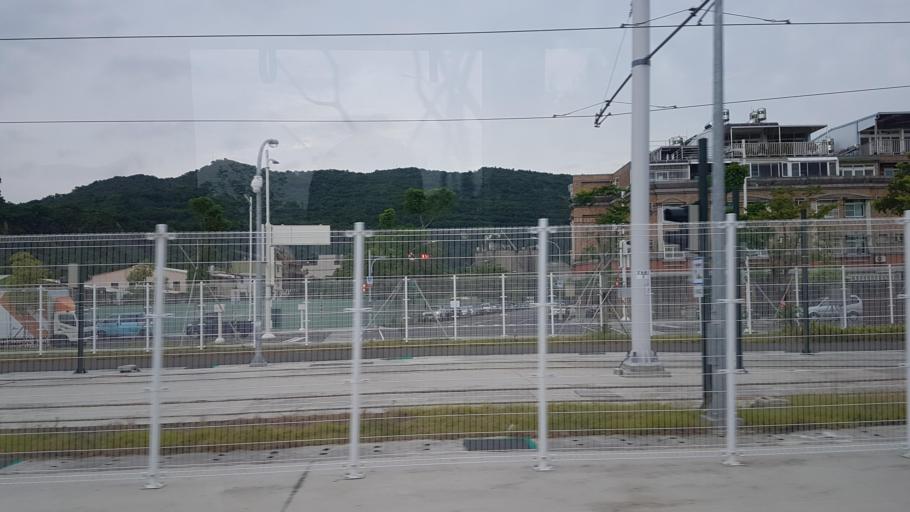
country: TW
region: Kaohsiung
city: Kaohsiung
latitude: 22.6445
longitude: 120.2812
